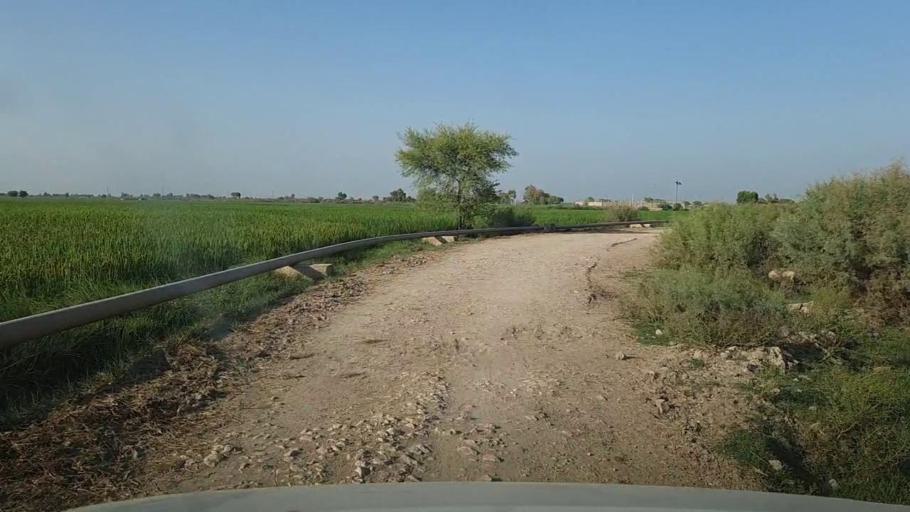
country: PK
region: Sindh
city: Kandhkot
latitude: 28.2955
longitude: 69.3266
